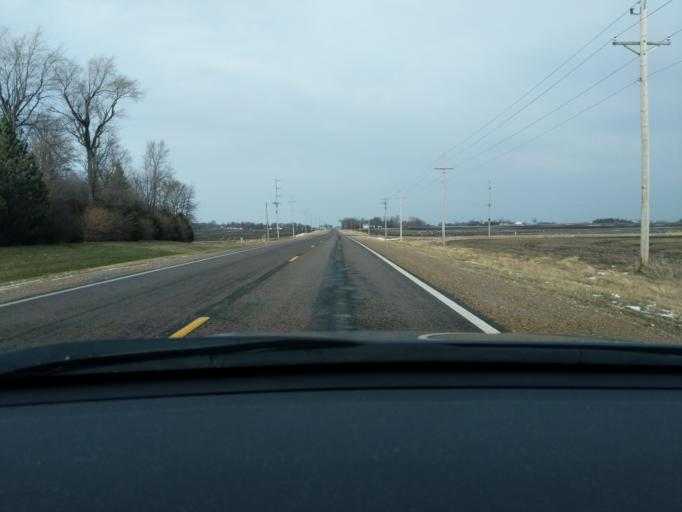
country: US
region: Minnesota
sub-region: Renville County
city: Renville
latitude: 44.7733
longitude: -95.3408
